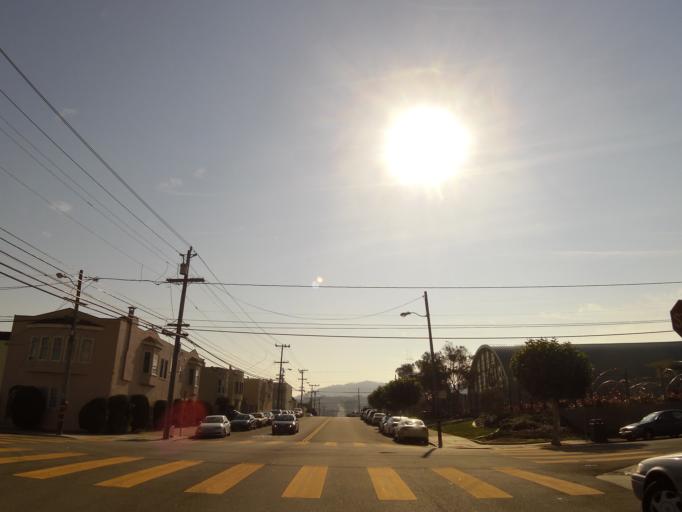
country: US
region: California
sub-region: San Mateo County
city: Daly City
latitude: 37.7575
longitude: -122.4877
